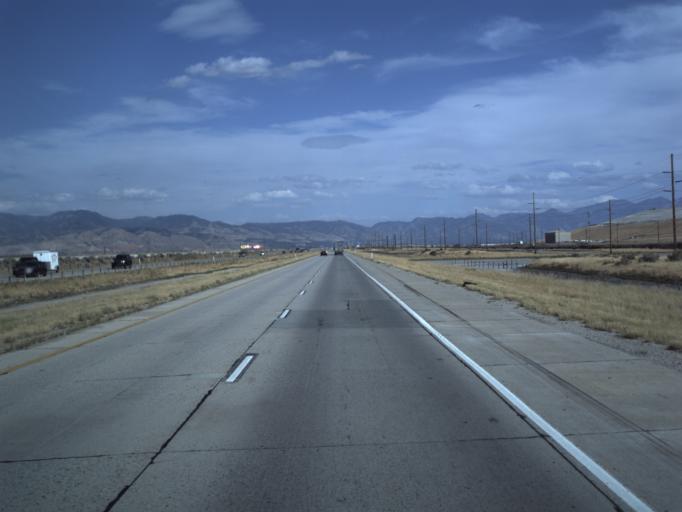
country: US
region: Utah
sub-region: Salt Lake County
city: Magna
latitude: 40.7707
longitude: -112.1155
